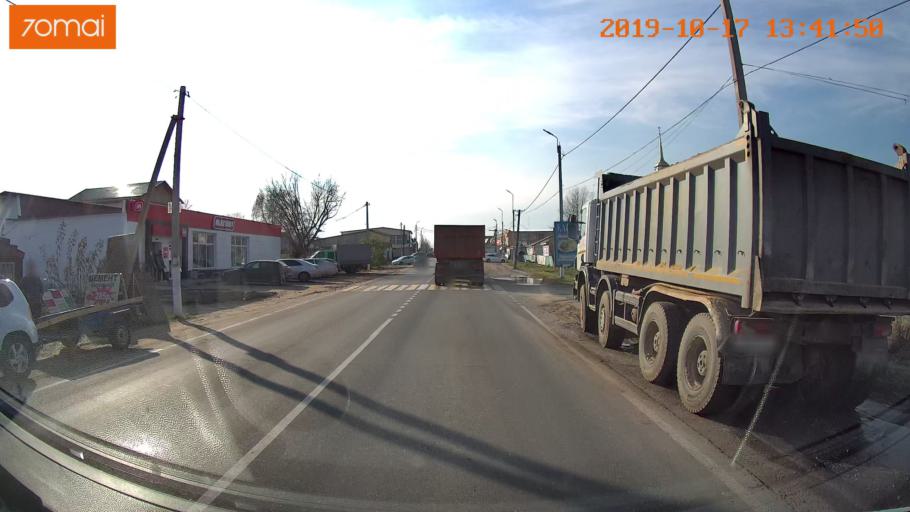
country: RU
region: Rjazan
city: Tuma
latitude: 55.1484
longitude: 40.5596
